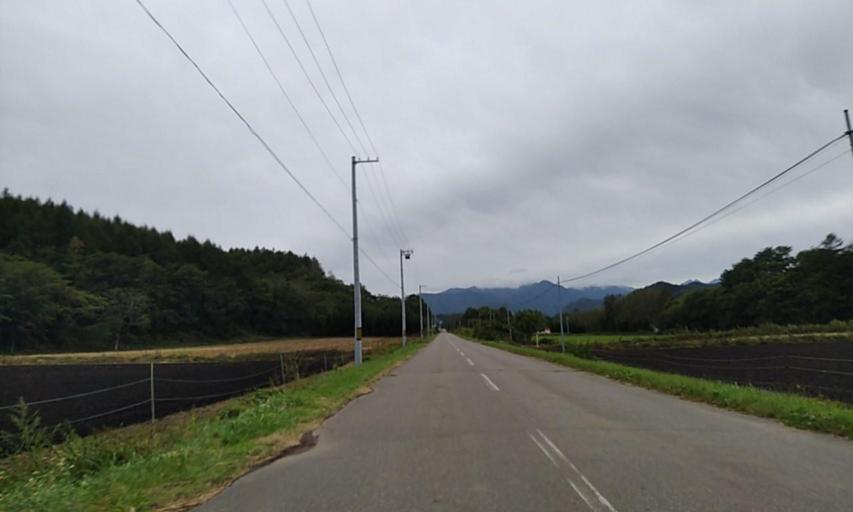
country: JP
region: Hokkaido
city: Obihiro
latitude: 42.6700
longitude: 143.0385
